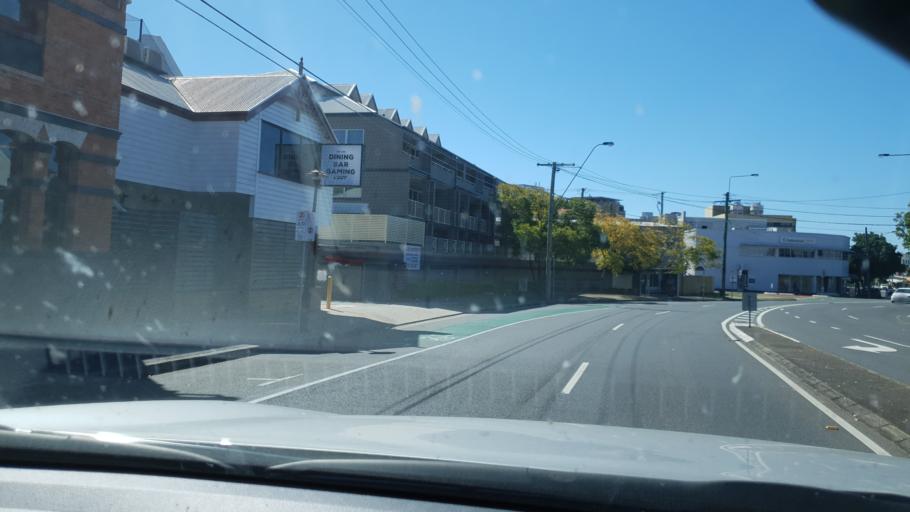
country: AU
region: Queensland
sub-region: Brisbane
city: Woolloongabba
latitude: -27.4899
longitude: 153.0272
